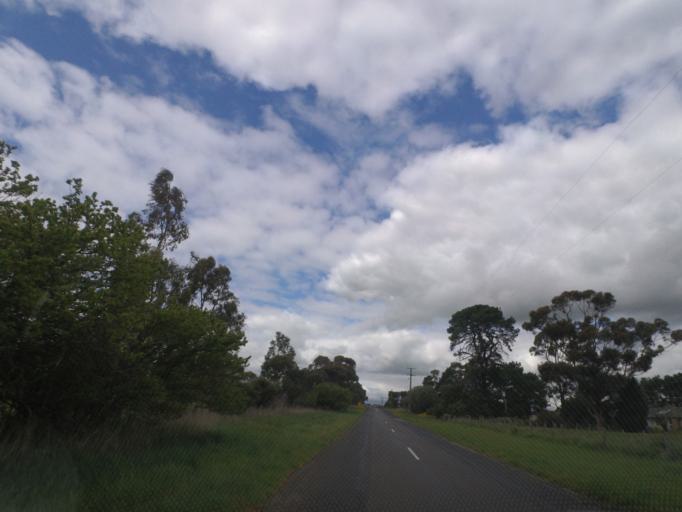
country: AU
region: Victoria
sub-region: Hume
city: Craigieburn
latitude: -37.4661
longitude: 144.9449
